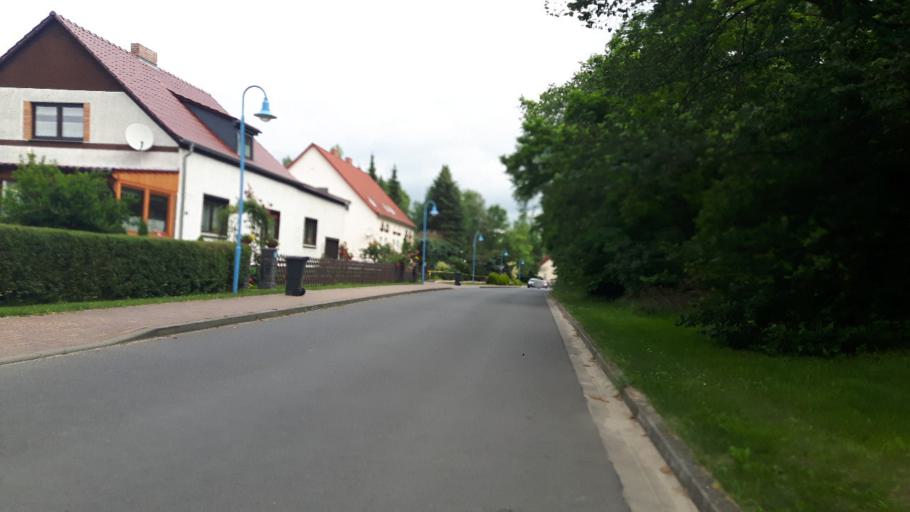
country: DE
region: Brandenburg
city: Mescherin
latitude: 53.2456
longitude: 14.4276
